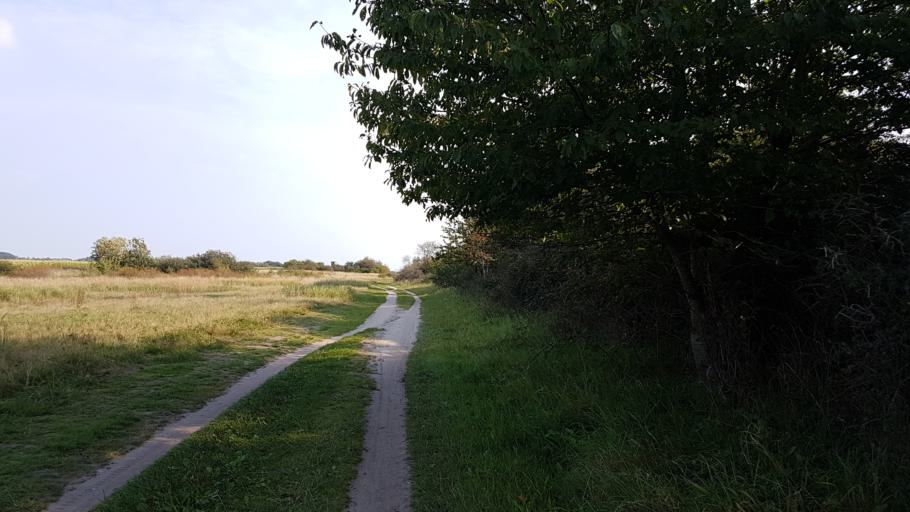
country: DE
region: Mecklenburg-Vorpommern
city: Glowe
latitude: 54.5566
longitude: 13.4972
